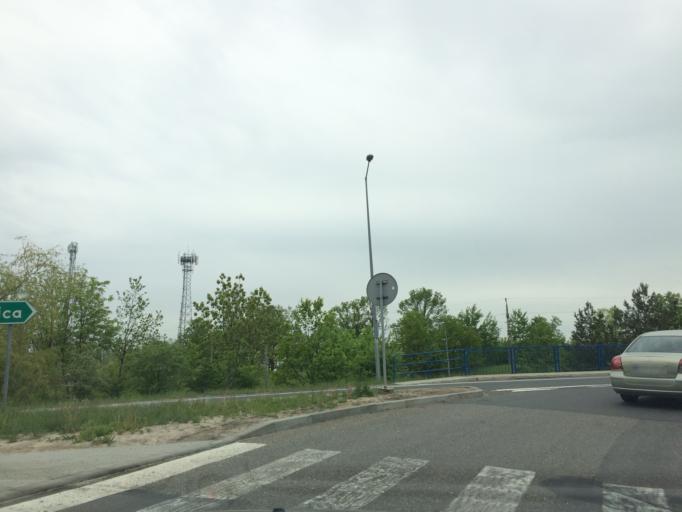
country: PL
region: Lower Silesian Voivodeship
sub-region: Powiat legnicki
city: Prochowice
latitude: 51.2721
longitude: 16.3547
